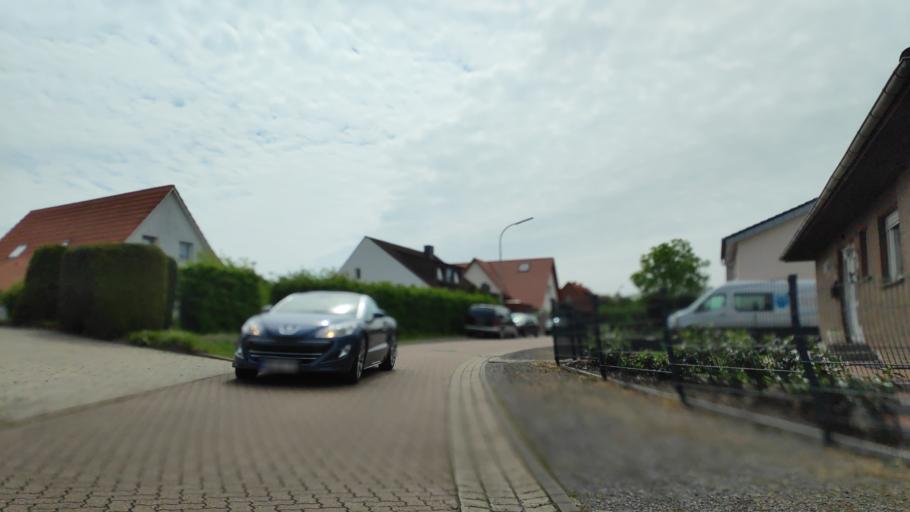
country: DE
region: North Rhine-Westphalia
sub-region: Regierungsbezirk Detmold
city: Petershagen
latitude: 52.3097
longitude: 8.9952
